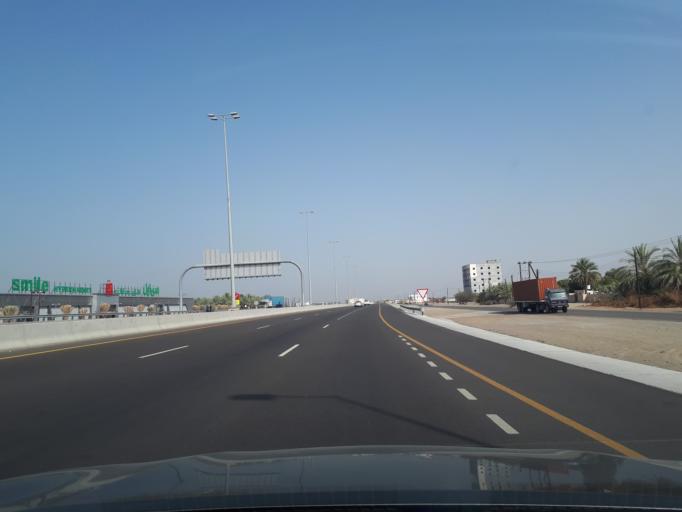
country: OM
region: Al Batinah
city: Al Sohar
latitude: 24.4176
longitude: 56.6267
